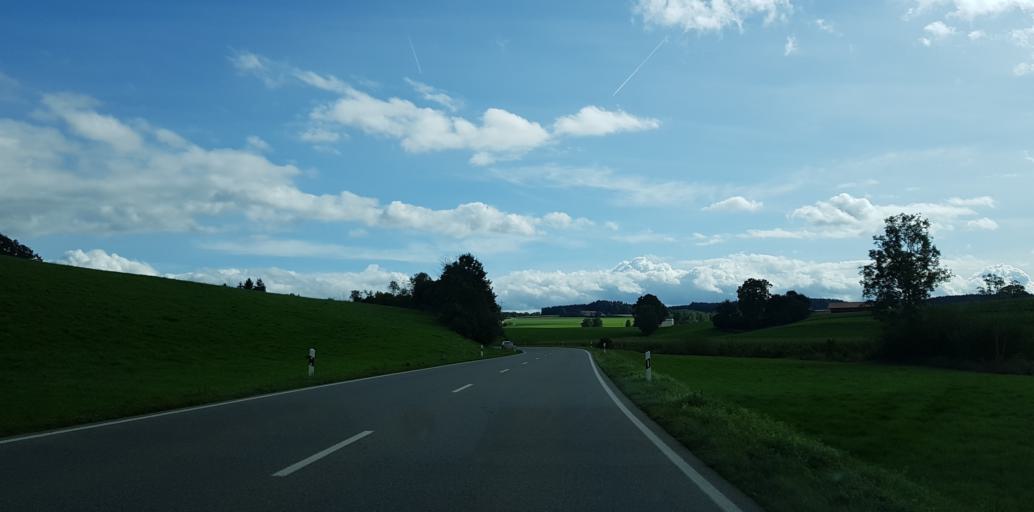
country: DE
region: Baden-Wuerttemberg
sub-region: Tuebingen Region
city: Eberhardzell
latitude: 47.9559
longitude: 9.8433
